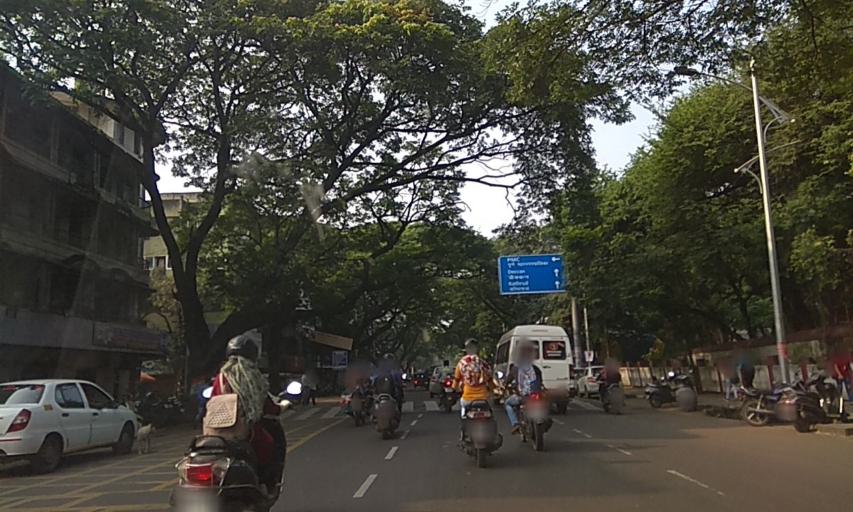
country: IN
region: Maharashtra
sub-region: Pune Division
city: Shivaji Nagar
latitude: 18.5266
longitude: 73.8506
